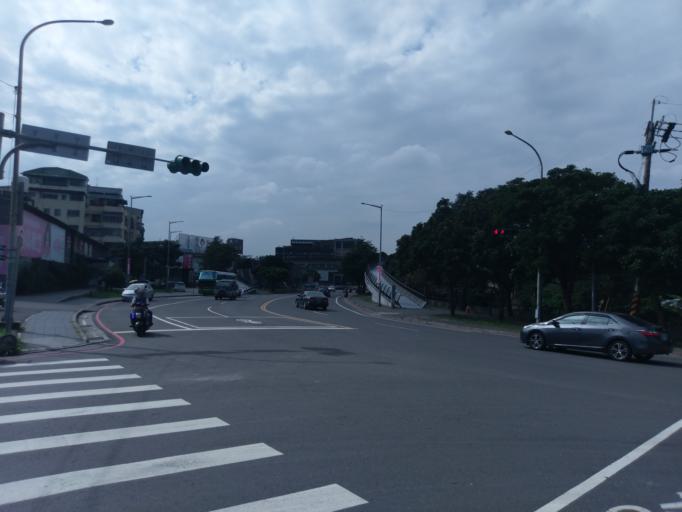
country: TW
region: Taiwan
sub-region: Taoyuan
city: Taoyuan
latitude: 24.9503
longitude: 121.3543
